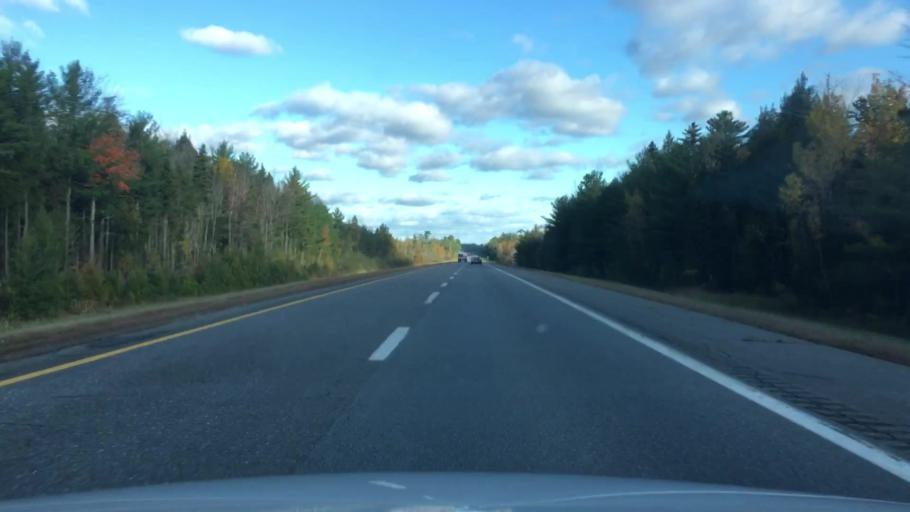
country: US
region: Maine
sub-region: Penobscot County
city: Greenbush
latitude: 45.1269
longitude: -68.6955
